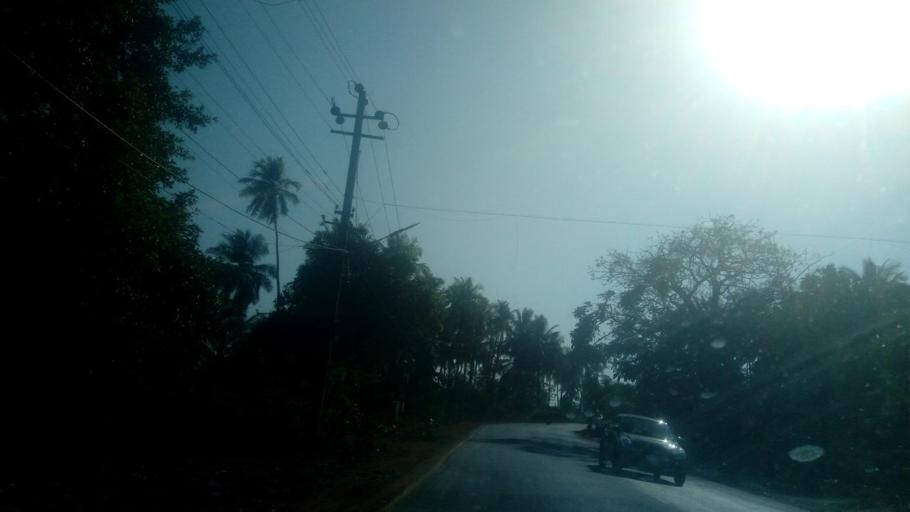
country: IN
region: Goa
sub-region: North Goa
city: Jua
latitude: 15.5005
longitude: 73.9626
